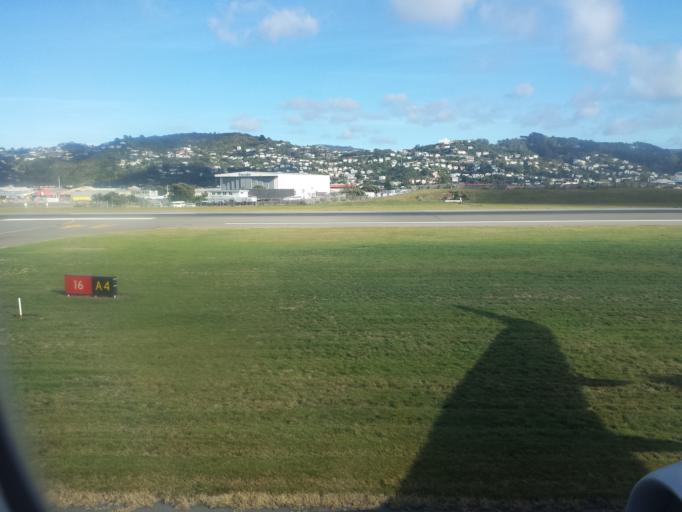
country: NZ
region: Wellington
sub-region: Wellington City
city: Wellington
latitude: -41.3238
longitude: 174.8083
